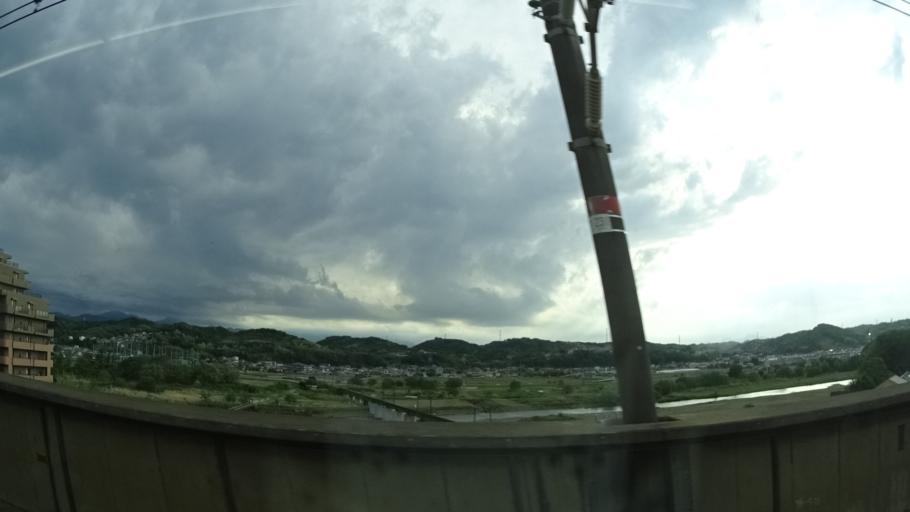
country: JP
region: Gunma
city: Takasaki
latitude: 36.3032
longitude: 139.0183
